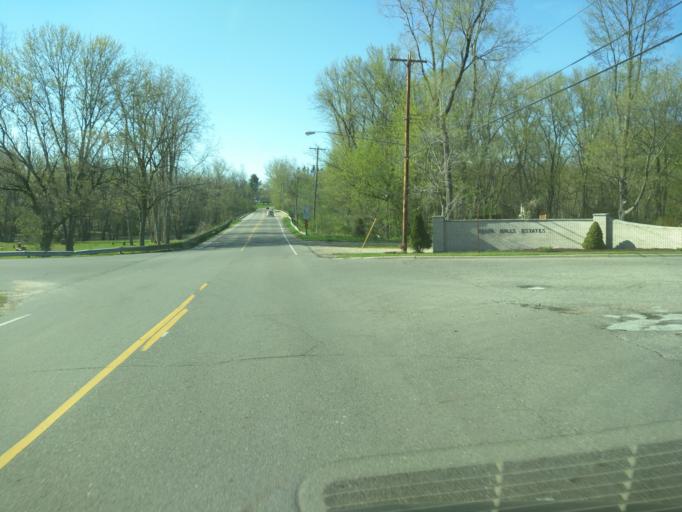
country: US
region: Michigan
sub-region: Eaton County
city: Waverly
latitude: 42.7599
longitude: -84.6480
